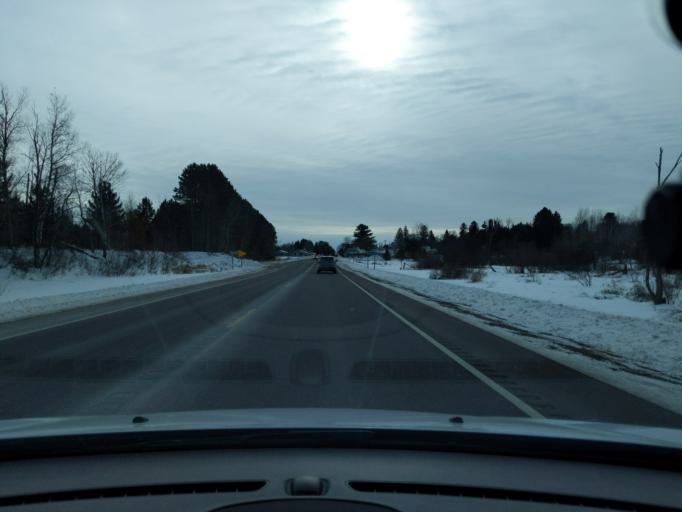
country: US
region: Wisconsin
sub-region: Barron County
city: Cumberland
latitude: 45.6404
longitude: -91.9928
